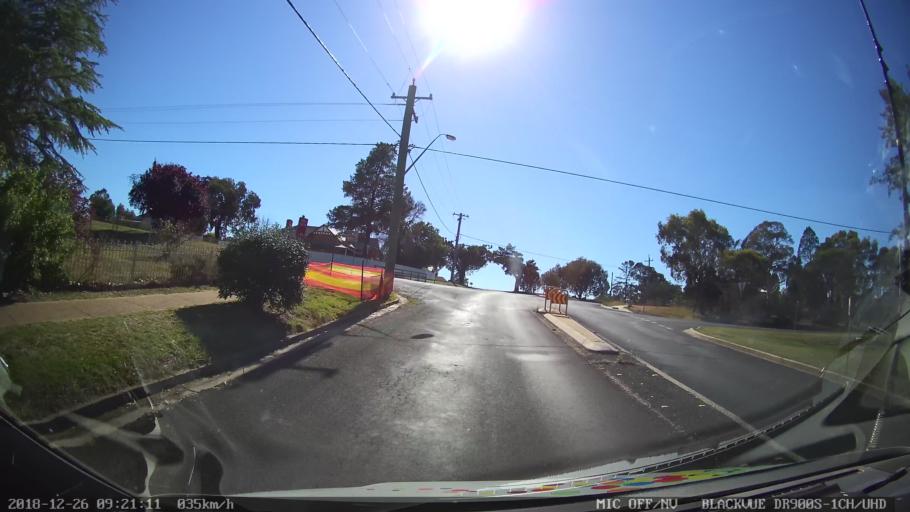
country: AU
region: New South Wales
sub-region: Mid-Western Regional
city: Kandos
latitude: -32.7991
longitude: 149.9721
